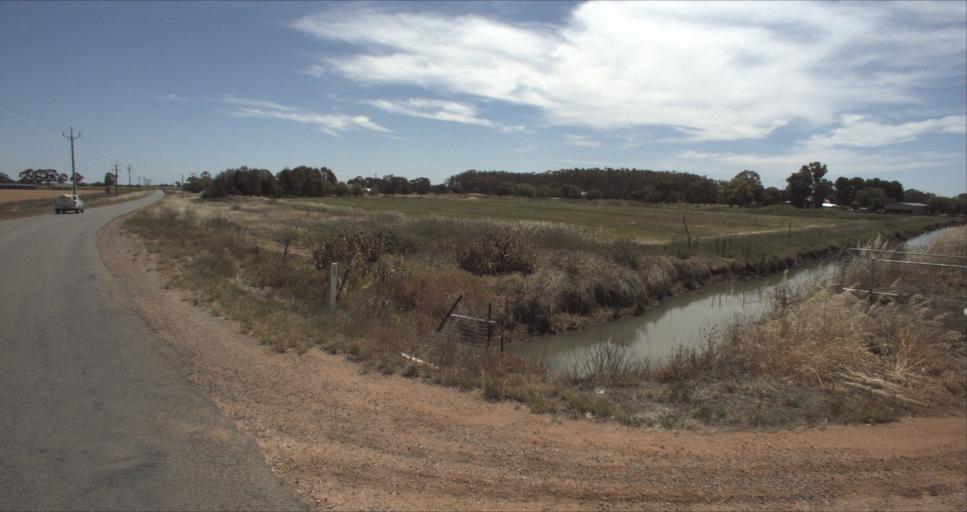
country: AU
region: New South Wales
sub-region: Leeton
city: Leeton
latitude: -34.5862
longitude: 146.4224
